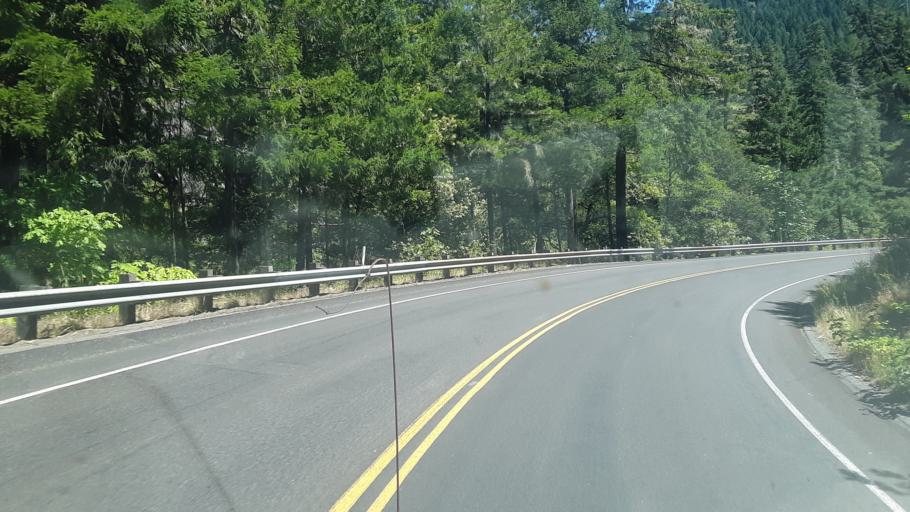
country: US
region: Oregon
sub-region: Josephine County
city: Cave Junction
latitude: 41.8839
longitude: -123.8258
